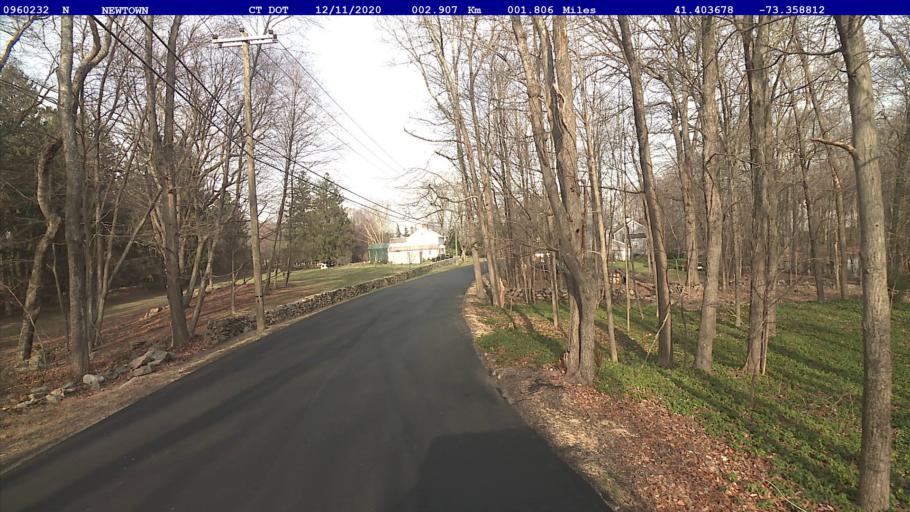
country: US
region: Connecticut
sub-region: Fairfield County
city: Newtown
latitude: 41.4037
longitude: -73.3589
